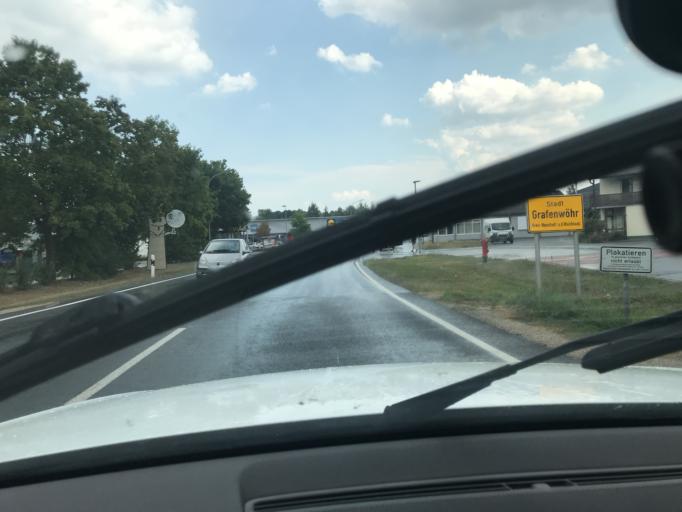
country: DE
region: Bavaria
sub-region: Upper Palatinate
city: Grafenwohr
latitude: 49.7304
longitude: 11.9028
